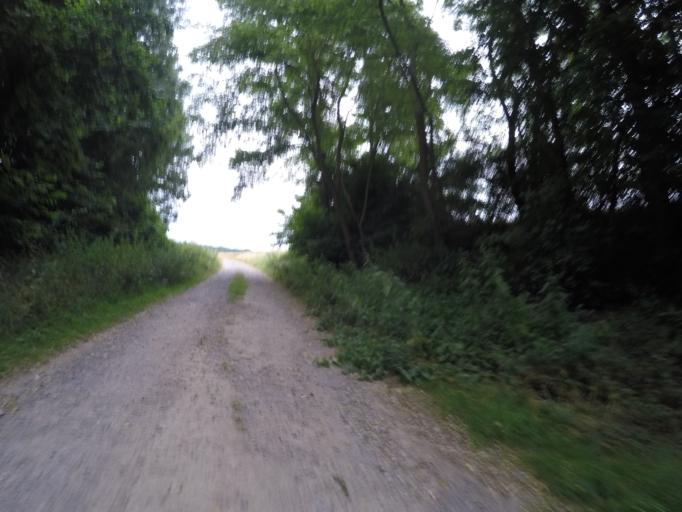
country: BE
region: Wallonia
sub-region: Province de Namur
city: Assesse
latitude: 50.2979
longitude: 5.0195
